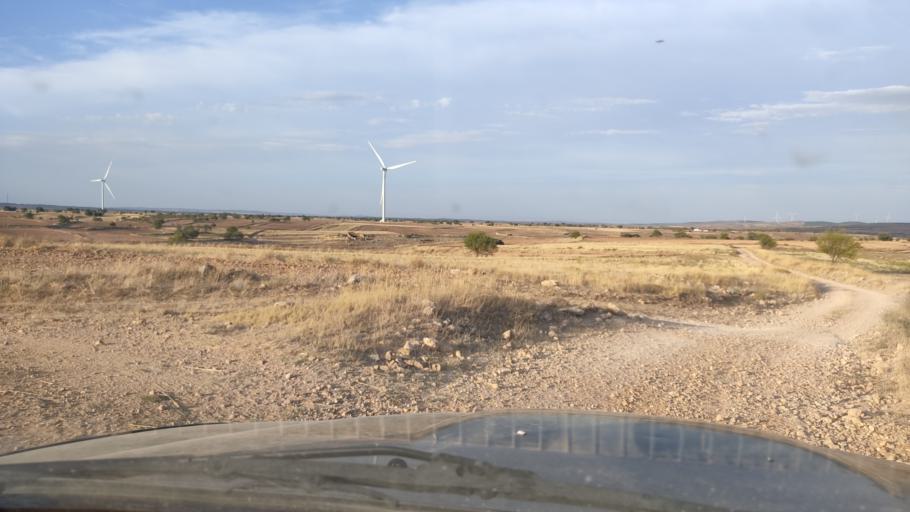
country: ES
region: Aragon
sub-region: Provincia de Teruel
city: Monforte de Moyuela
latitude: 41.0681
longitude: -0.9932
